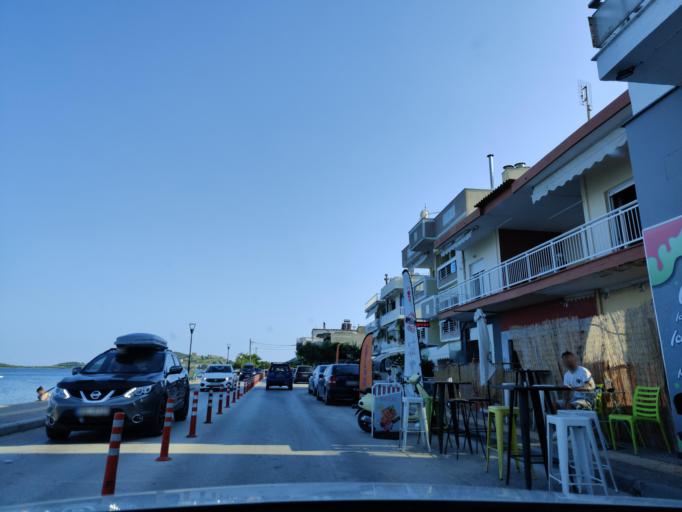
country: GR
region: East Macedonia and Thrace
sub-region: Nomos Kavalas
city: Nea Peramos
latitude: 40.8371
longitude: 24.3052
